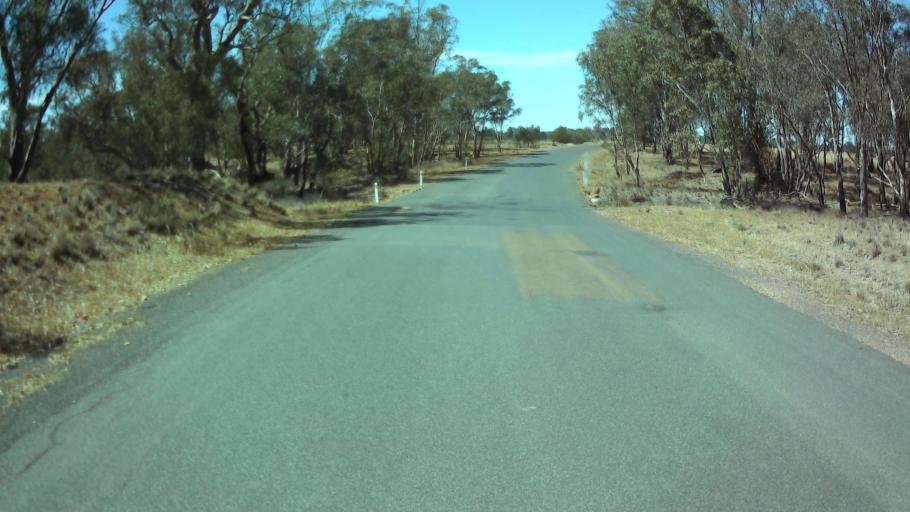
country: AU
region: New South Wales
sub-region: Weddin
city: Grenfell
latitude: -34.1016
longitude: 147.8874
